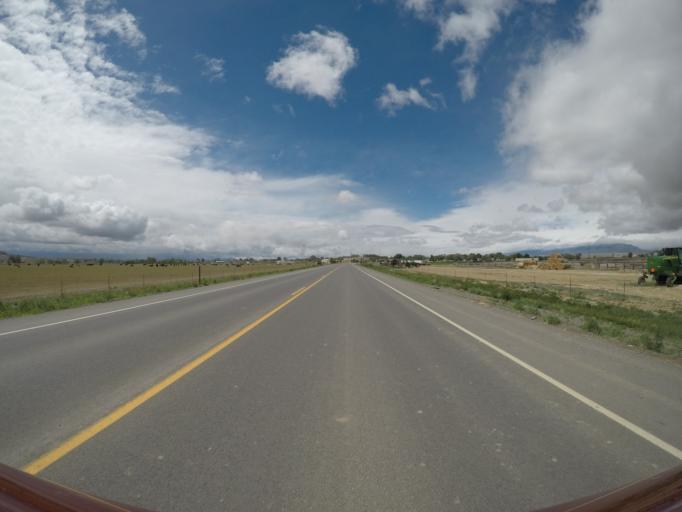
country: US
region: Wyoming
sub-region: Big Horn County
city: Lovell
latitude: 44.8721
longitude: -108.4593
